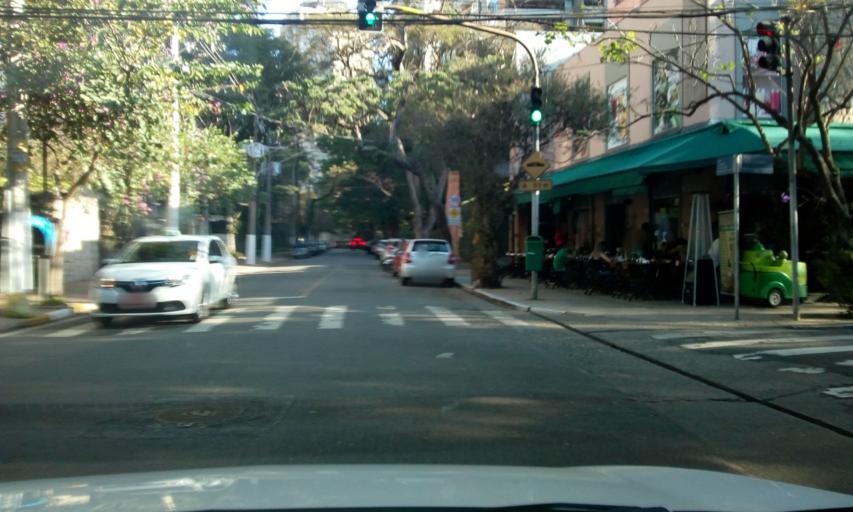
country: BR
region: Sao Paulo
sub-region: Sao Paulo
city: Sao Paulo
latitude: -23.5909
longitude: -46.6673
